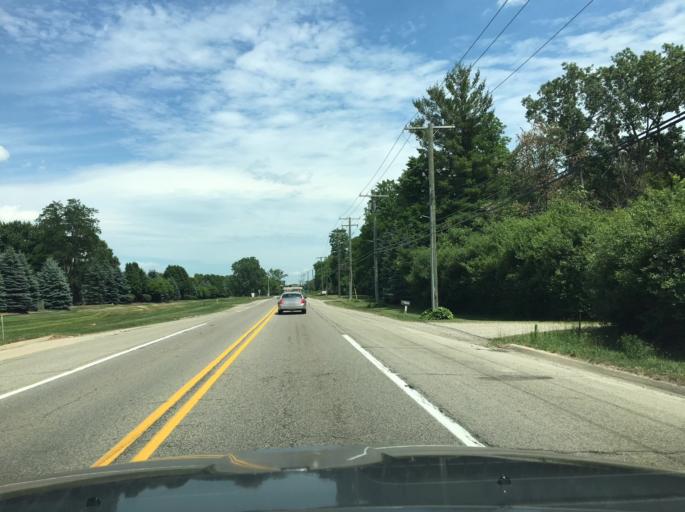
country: US
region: Michigan
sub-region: Macomb County
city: Shelby
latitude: 42.7146
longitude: -83.0005
